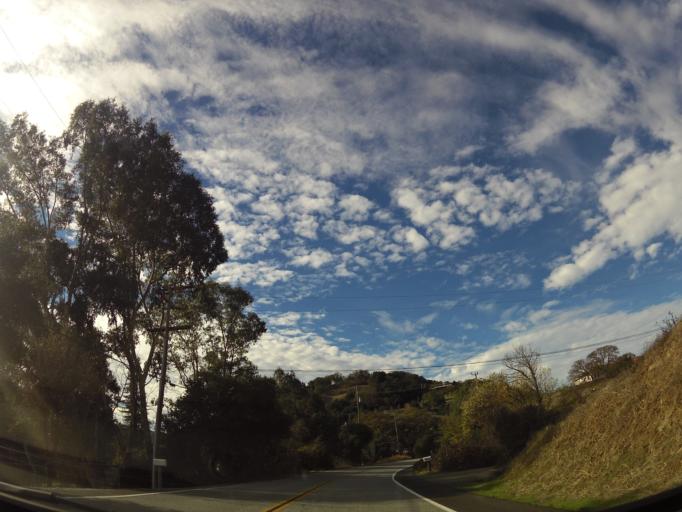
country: US
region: California
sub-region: Santa Clara County
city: Morgan Hill
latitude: 37.1506
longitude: -121.7465
